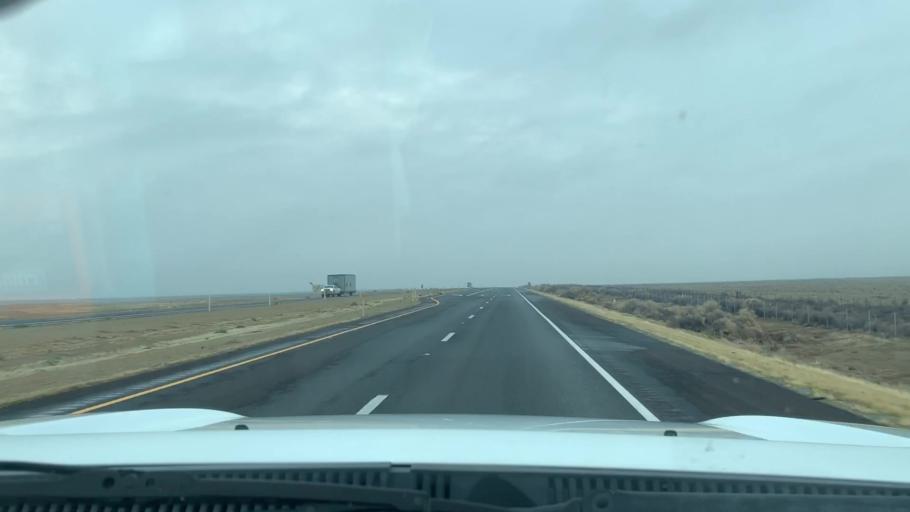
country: US
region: California
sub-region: Kern County
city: Lost Hills
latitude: 35.6333
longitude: -120.0042
